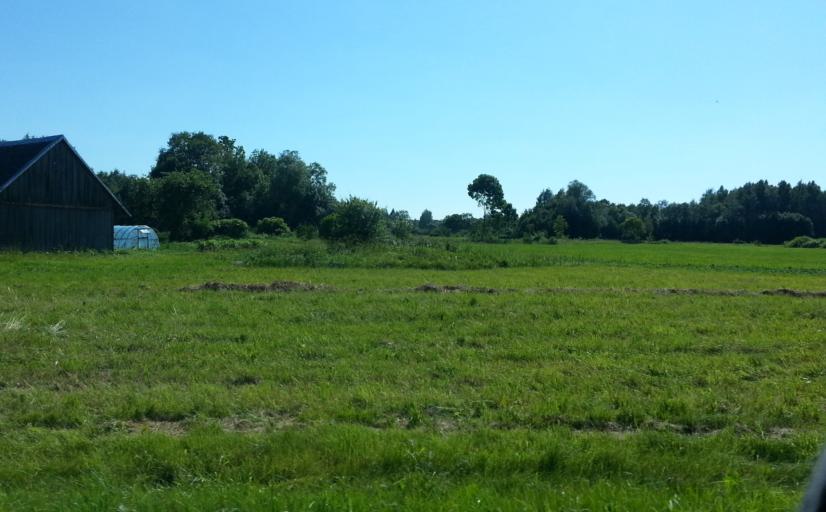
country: LT
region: Panevezys
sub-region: Birzai
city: Birzai
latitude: 56.2242
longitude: 24.7016
